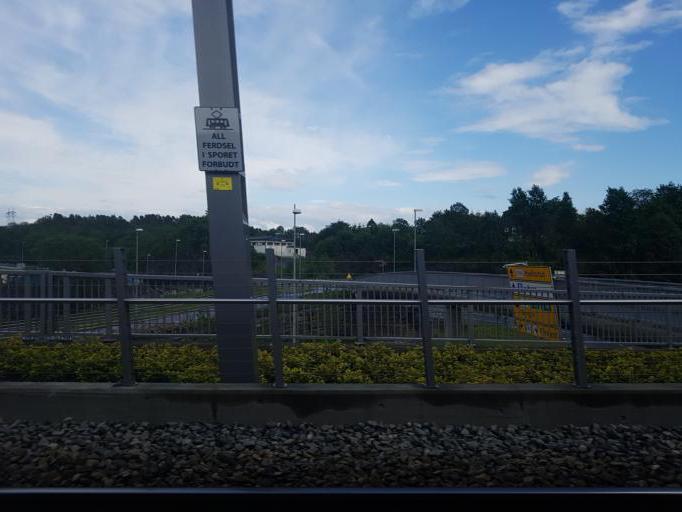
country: NO
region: Hordaland
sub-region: Bergen
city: Ytrebygda
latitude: 60.2893
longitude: 5.2640
